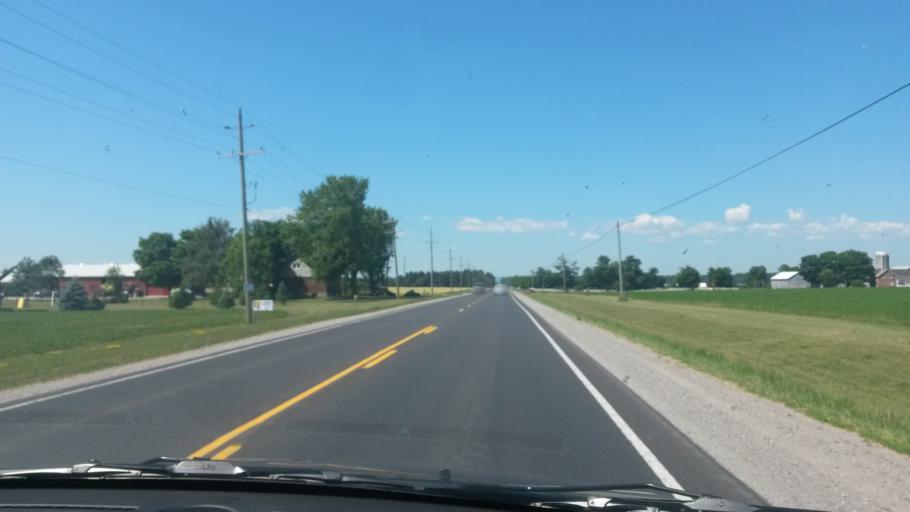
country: CA
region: Ontario
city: Barrie
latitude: 44.5058
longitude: -79.7778
